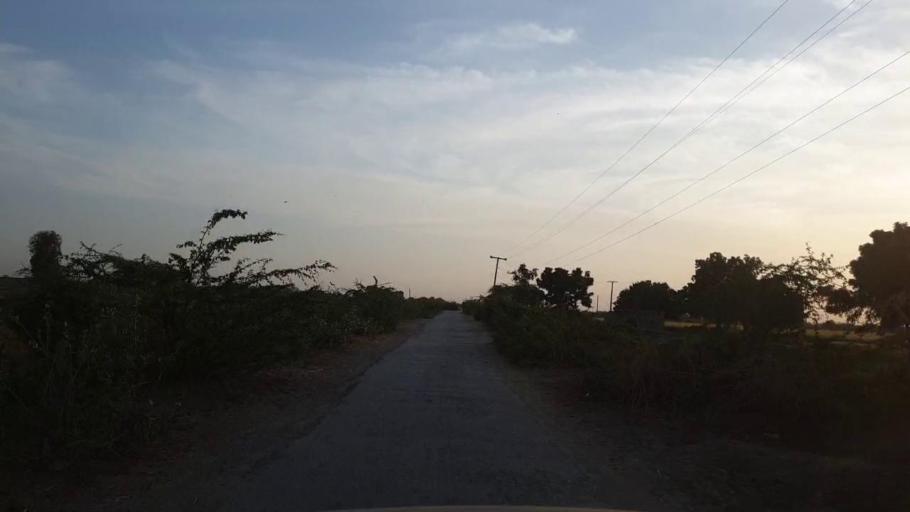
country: PK
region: Sindh
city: Kunri
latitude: 25.1380
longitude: 69.5770
